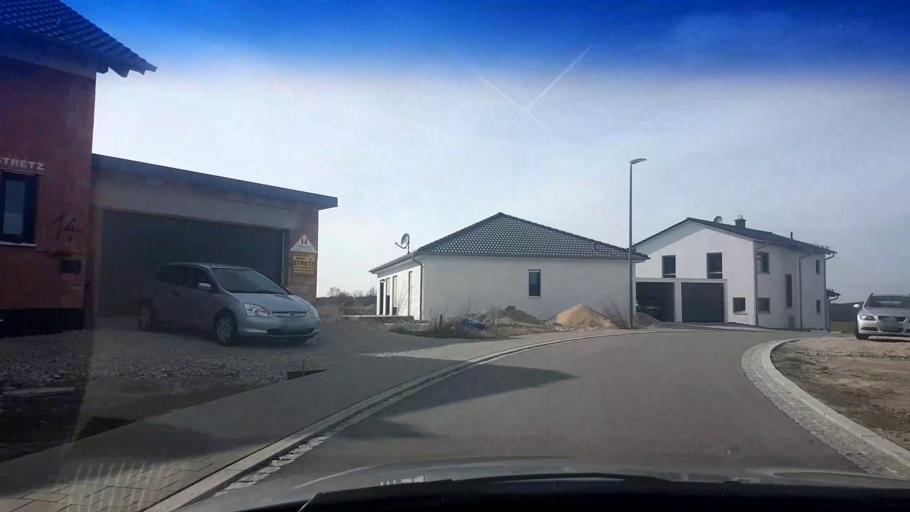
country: DE
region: Bavaria
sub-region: Upper Franconia
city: Burgebrach
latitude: 49.8183
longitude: 10.7392
